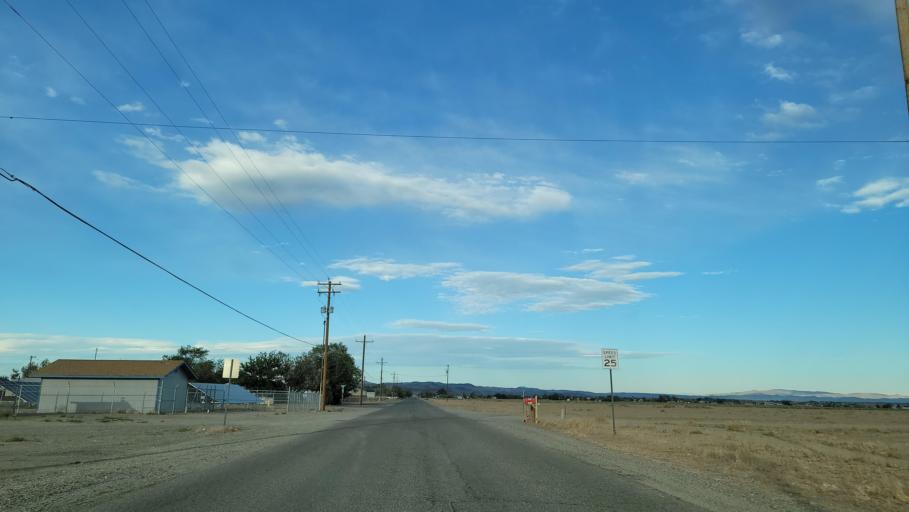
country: US
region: Nevada
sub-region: Lyon County
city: Silver Springs
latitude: 39.3900
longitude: -119.2506
